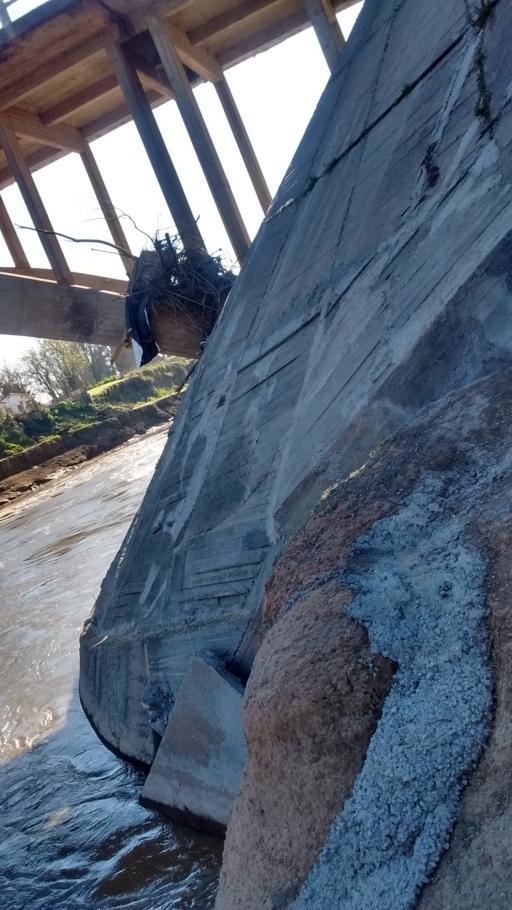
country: AR
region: Santa Fe
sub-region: Departamento de San Lorenzo
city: San Lorenzo
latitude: -32.6391
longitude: -60.8144
